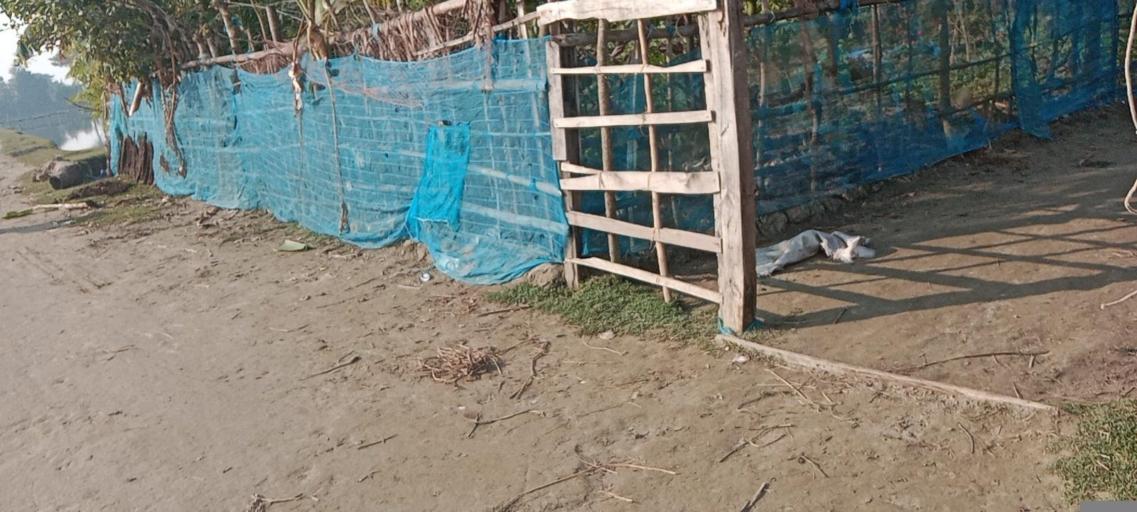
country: BD
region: Khulna
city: Phultala
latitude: 22.6078
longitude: 89.5877
